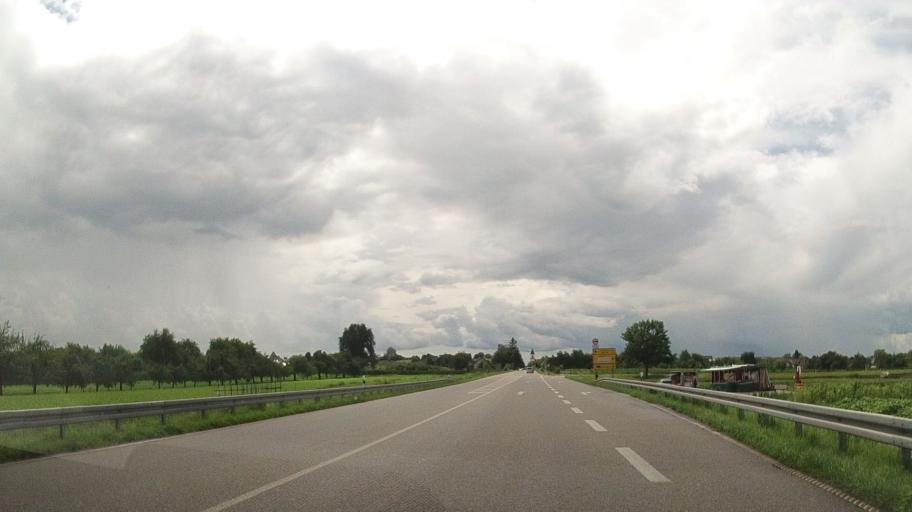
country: DE
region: Baden-Wuerttemberg
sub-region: Freiburg Region
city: Renchen
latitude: 48.5942
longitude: 8.0206
